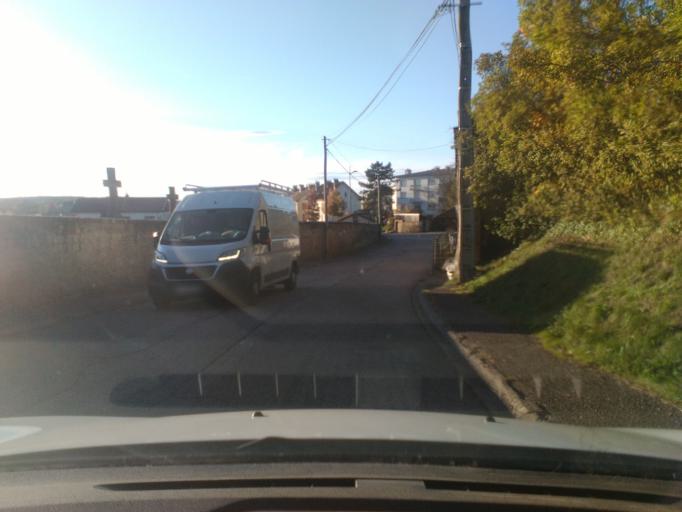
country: FR
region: Lorraine
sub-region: Departement des Vosges
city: Chatel-sur-Moselle
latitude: 48.3136
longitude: 6.3966
